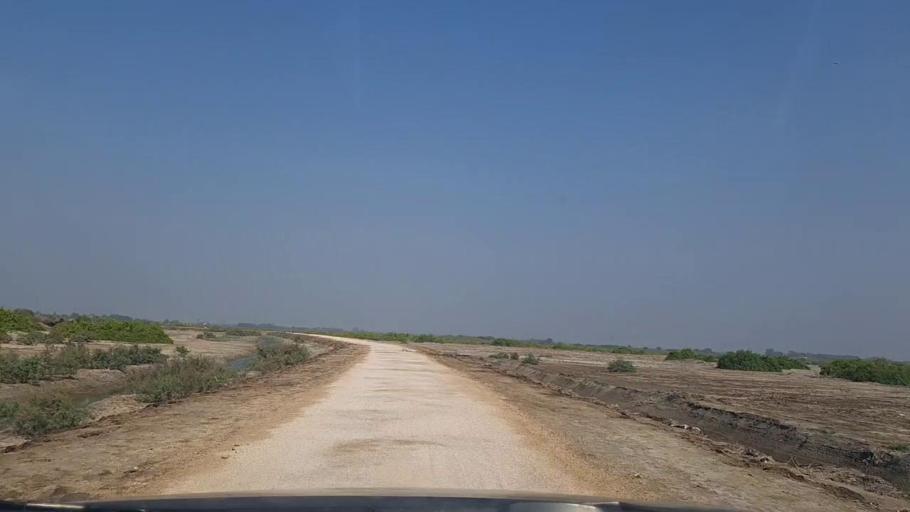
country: PK
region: Sindh
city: Mirpur Sakro
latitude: 24.5763
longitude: 67.7574
